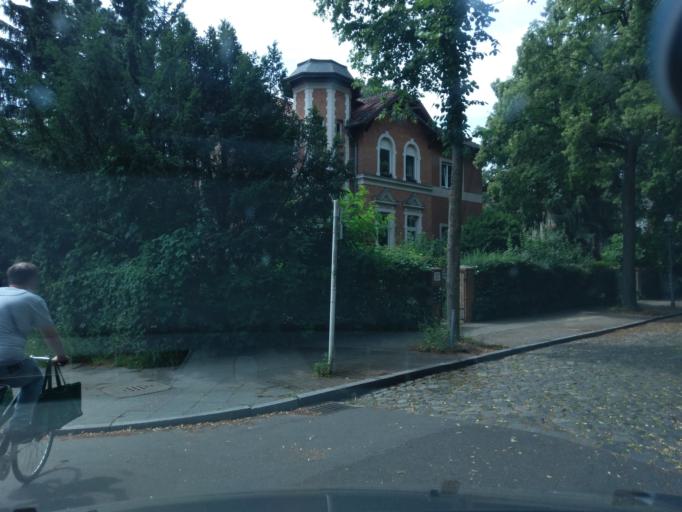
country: DE
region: Berlin
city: Lichterfelde
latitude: 52.4336
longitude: 13.2928
